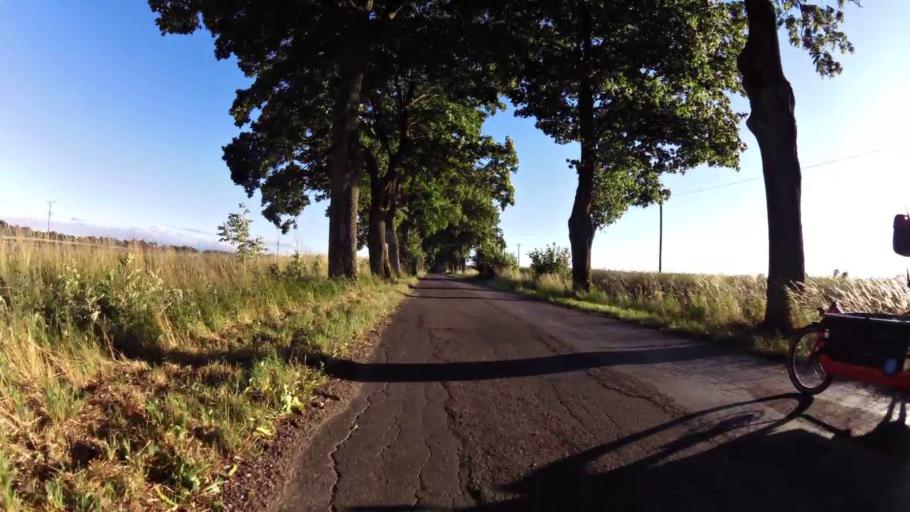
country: PL
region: West Pomeranian Voivodeship
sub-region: Powiat swidwinski
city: Swidwin
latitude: 53.7410
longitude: 15.6837
